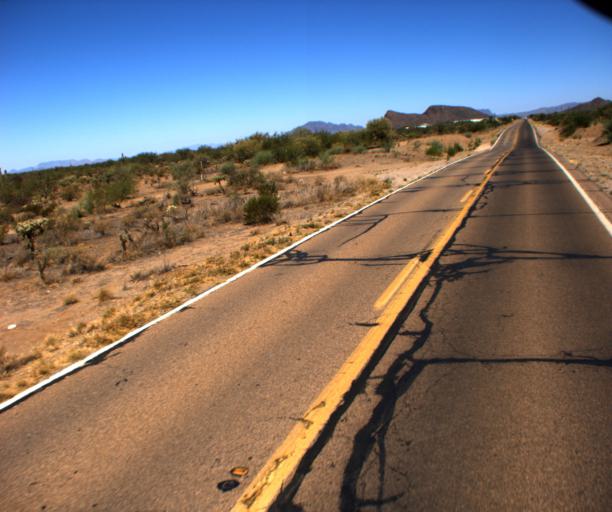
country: US
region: Arizona
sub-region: Pima County
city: Sells
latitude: 31.9297
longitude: -111.9057
